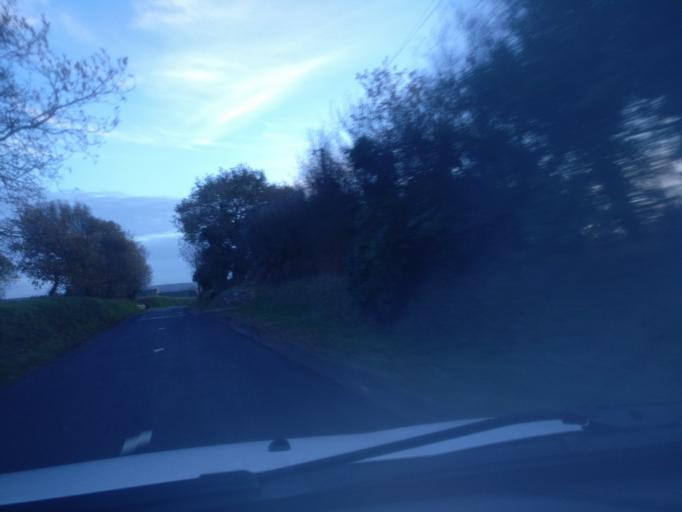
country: FR
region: Brittany
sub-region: Departement des Cotes-d'Armor
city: Saint-Quay-Perros
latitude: 48.8018
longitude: -3.4624
